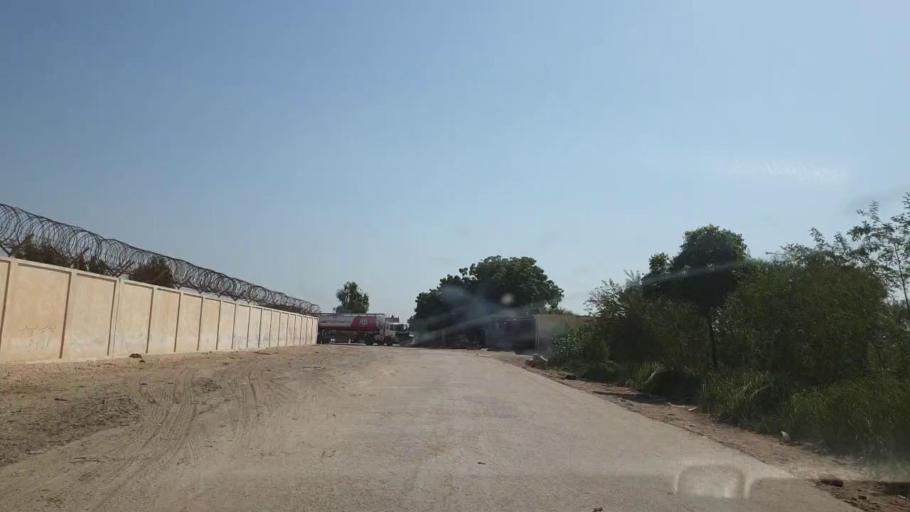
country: PK
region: Sindh
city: Tando Jam
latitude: 25.3837
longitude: 68.5791
